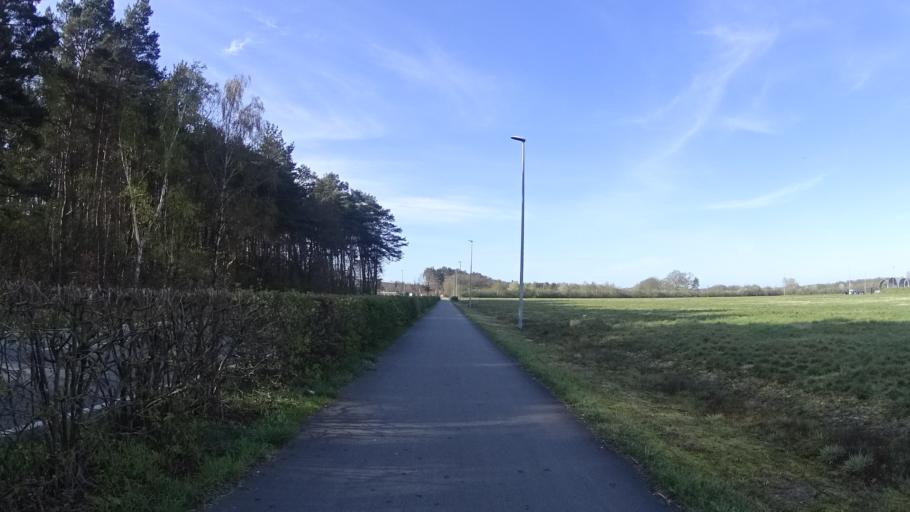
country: DE
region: Lower Saxony
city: Haren
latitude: 52.7736
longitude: 7.2756
